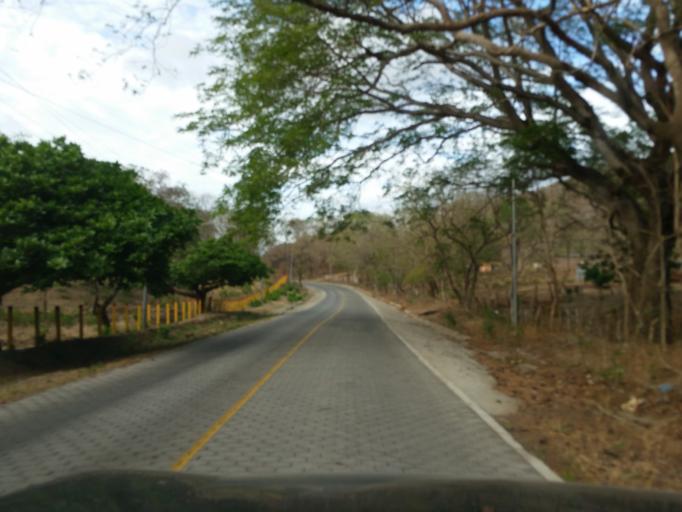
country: NI
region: Rivas
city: Tola
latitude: 11.4091
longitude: -85.9553
